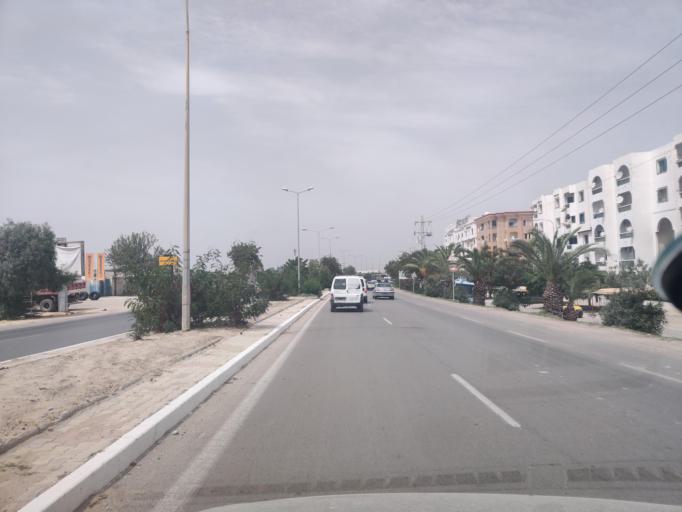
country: TN
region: Susah
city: Hammam Sousse
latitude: 35.8381
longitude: 10.5854
